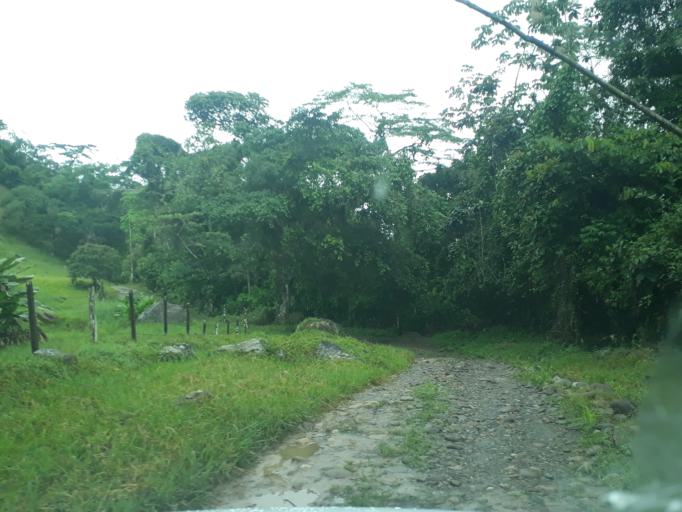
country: CO
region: Cundinamarca
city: Medina
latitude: 4.5260
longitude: -73.3643
